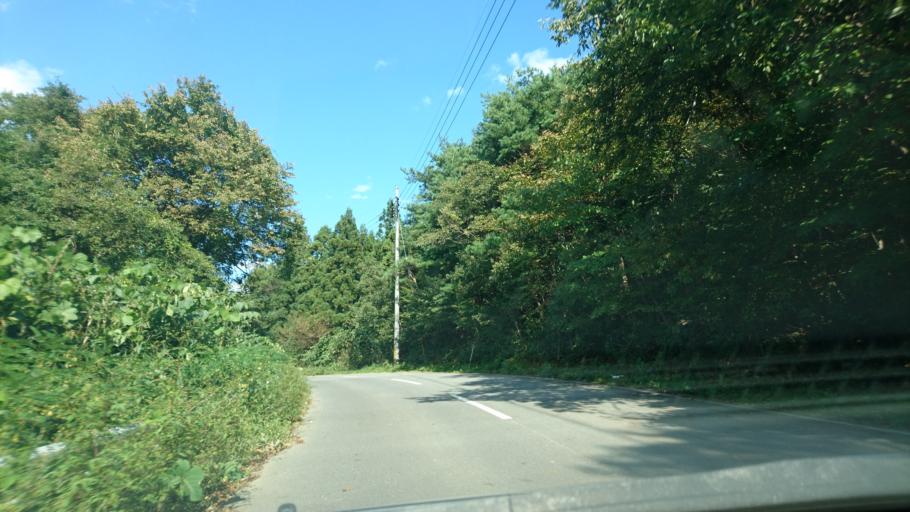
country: JP
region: Iwate
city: Ichinoseki
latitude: 38.8727
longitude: 141.0451
